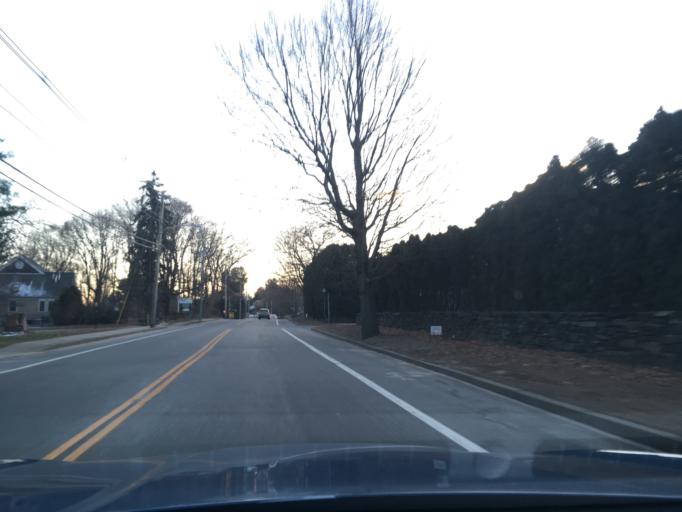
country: US
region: Rhode Island
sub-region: Kent County
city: East Greenwich
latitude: 41.6687
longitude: -71.4489
